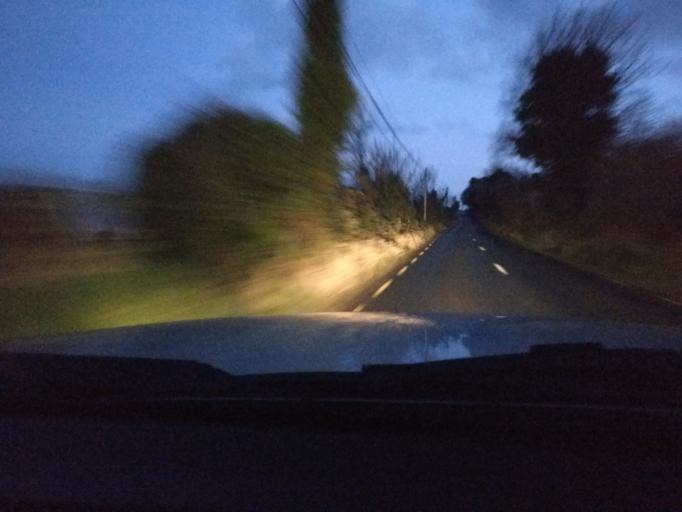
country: IE
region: Leinster
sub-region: Lu
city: Carlingford
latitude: 54.0597
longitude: -6.2043
